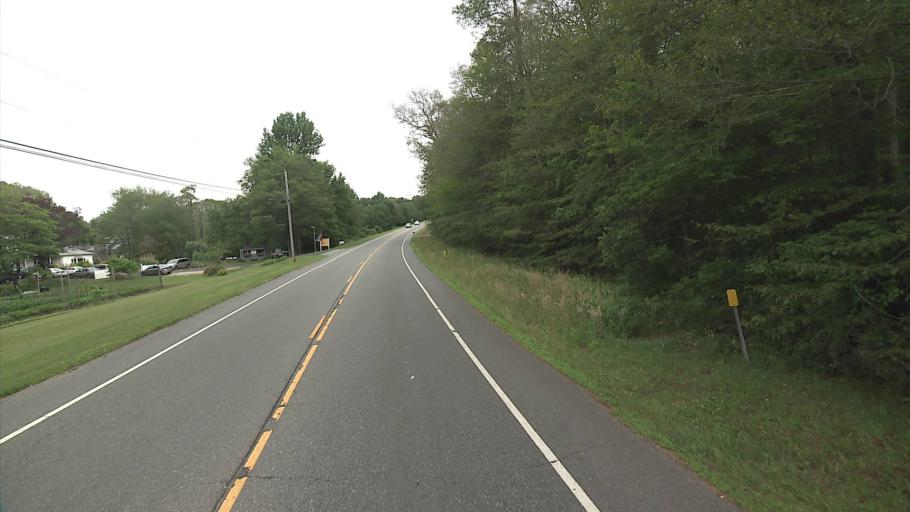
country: US
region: Connecticut
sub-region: New London County
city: Ledyard Center
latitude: 41.4022
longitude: -72.0254
